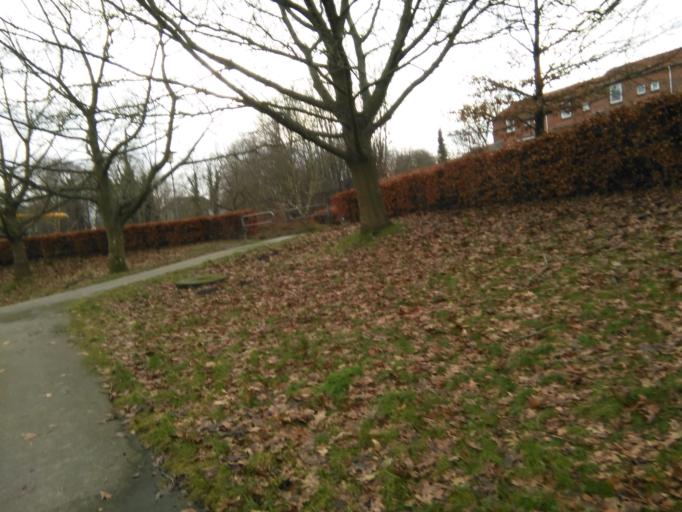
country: DK
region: Central Jutland
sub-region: Arhus Kommune
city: Stavtrup
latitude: 56.1538
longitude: 10.0873
